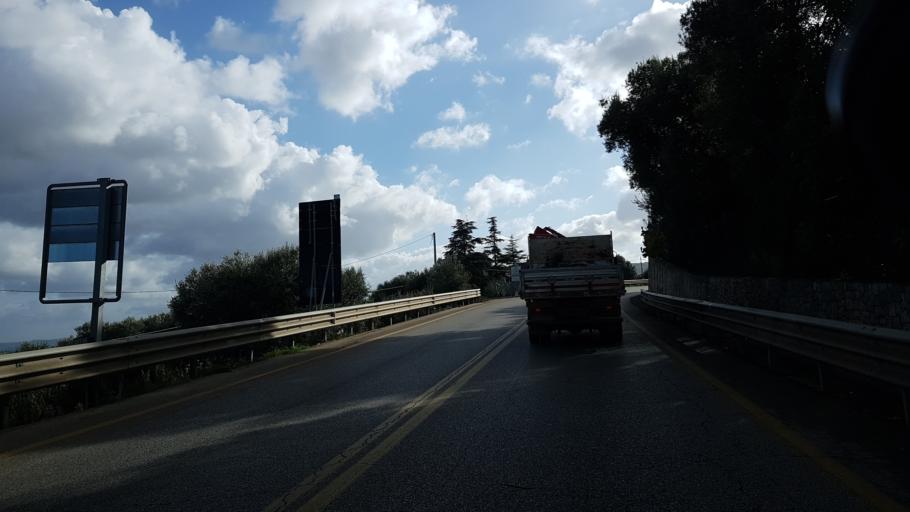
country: IT
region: Apulia
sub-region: Provincia di Brindisi
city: Fasano
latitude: 40.8286
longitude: 17.3506
